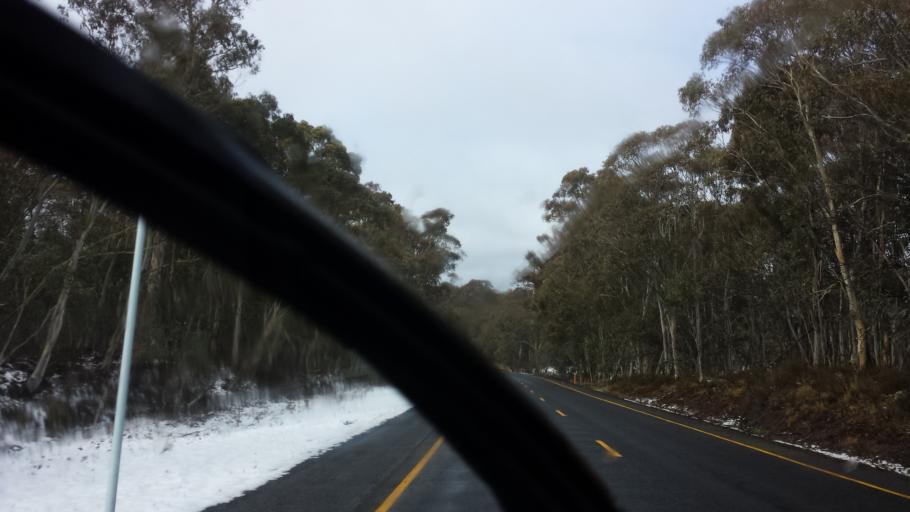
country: AU
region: Victoria
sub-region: Alpine
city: Mount Beauty
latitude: -37.0391
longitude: 147.3074
